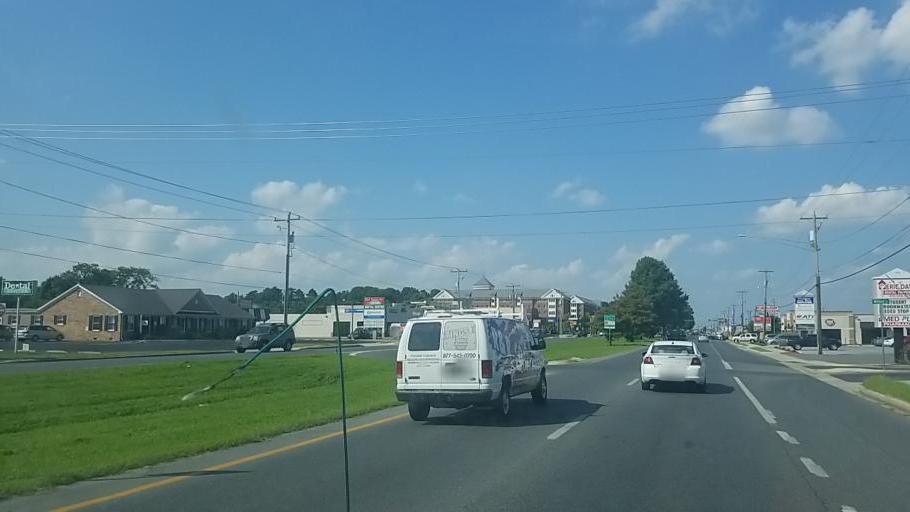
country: US
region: Maryland
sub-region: Wicomico County
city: Fruitland
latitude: 38.3391
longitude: -75.6063
